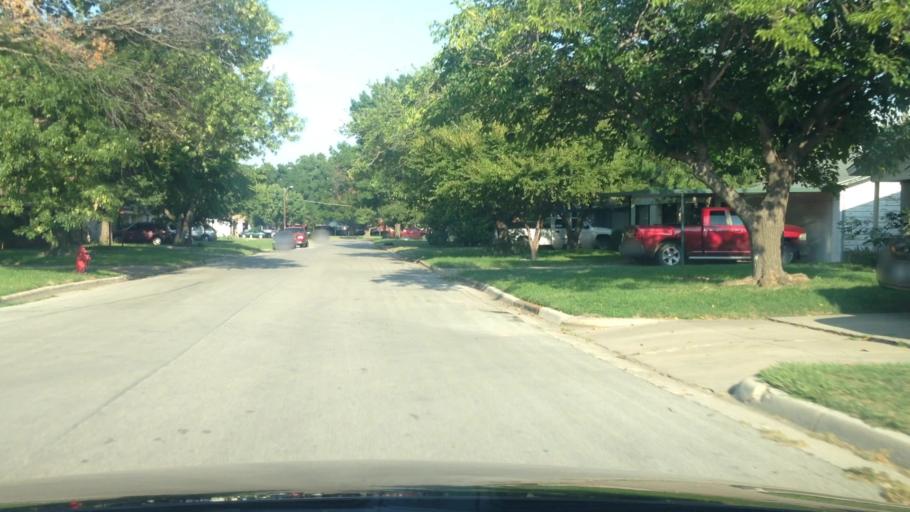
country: US
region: Texas
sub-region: Tarrant County
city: Everman
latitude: 32.6286
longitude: -97.2981
